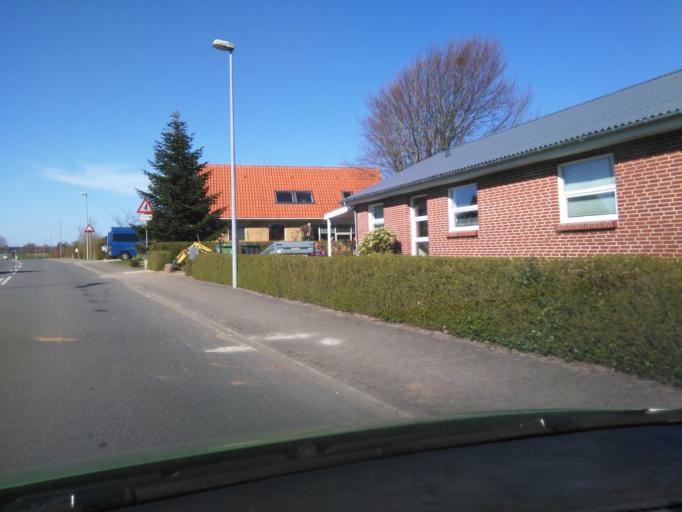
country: DK
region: South Denmark
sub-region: Varde Kommune
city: Oksbol
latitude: 55.6338
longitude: 8.2814
